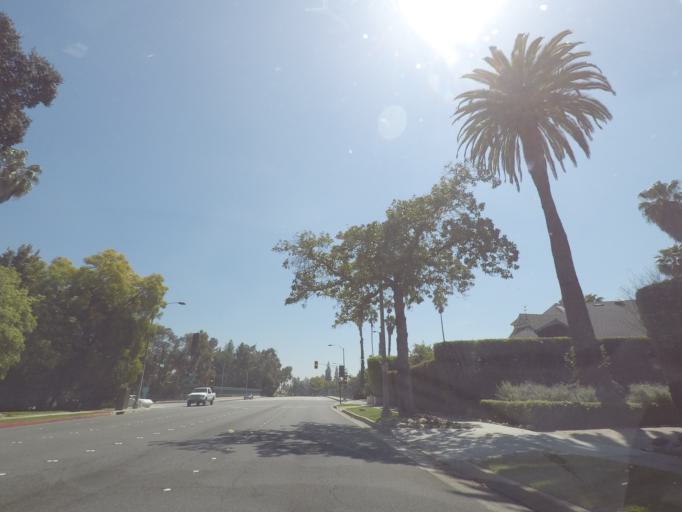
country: US
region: California
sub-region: Los Angeles County
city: Pasadena
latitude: 34.1479
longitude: -118.1616
